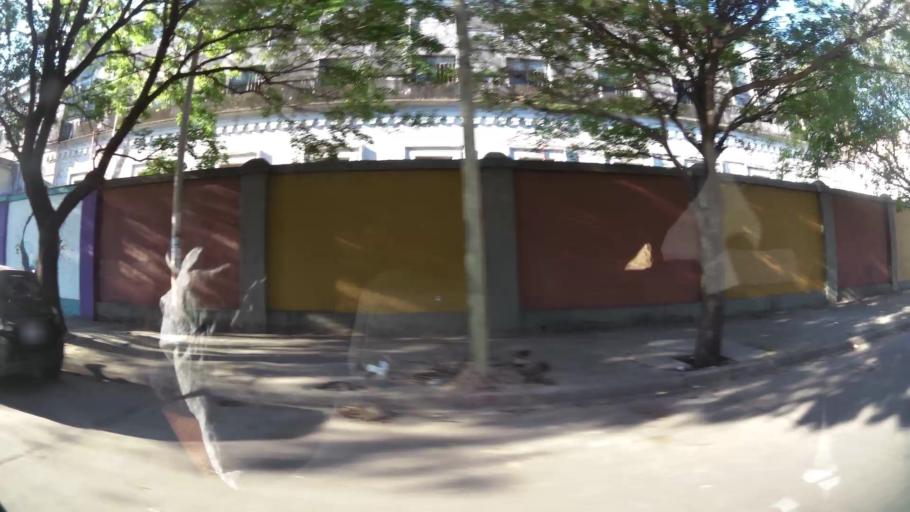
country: AR
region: Cordoba
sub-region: Departamento de Capital
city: Cordoba
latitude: -31.3887
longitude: -64.1843
